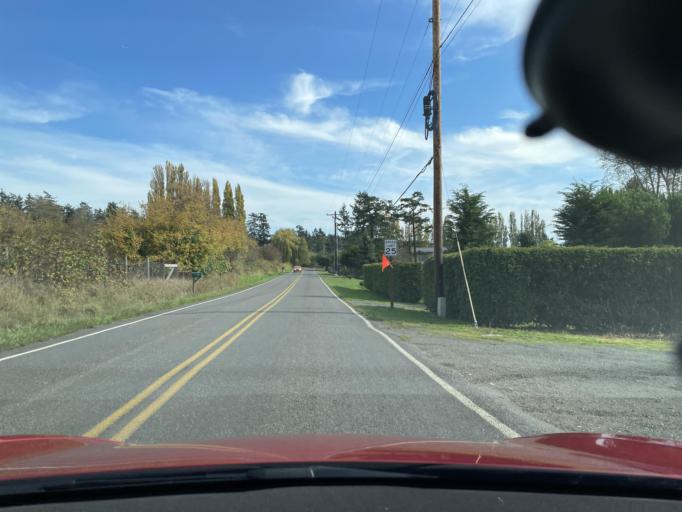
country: US
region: Washington
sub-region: San Juan County
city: Friday Harbor
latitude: 48.5229
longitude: -123.0171
